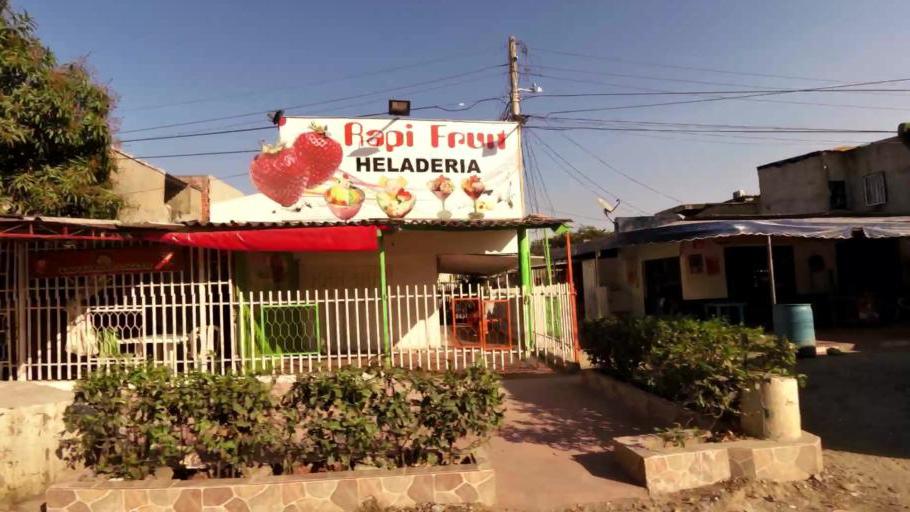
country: CO
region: Bolivar
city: Cartagena
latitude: 10.3822
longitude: -75.4836
